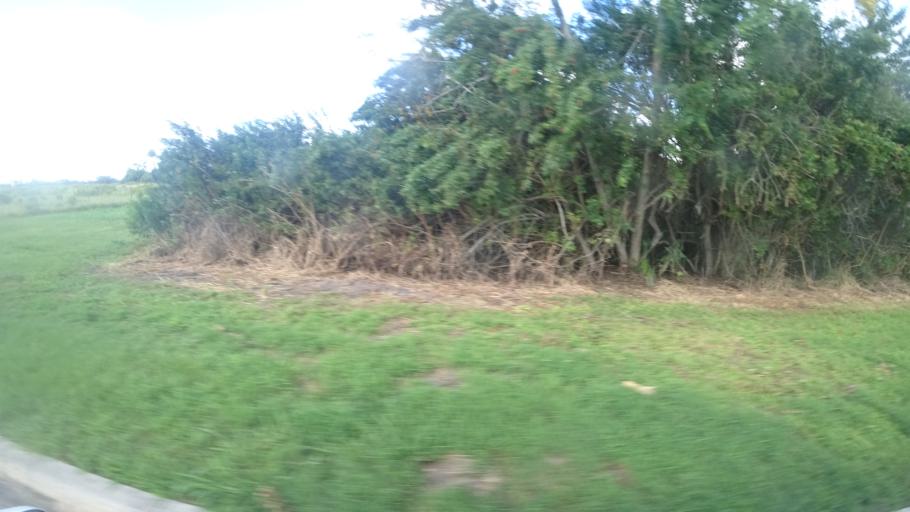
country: US
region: Florida
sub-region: Manatee County
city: Palmetto
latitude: 27.5336
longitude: -82.5747
